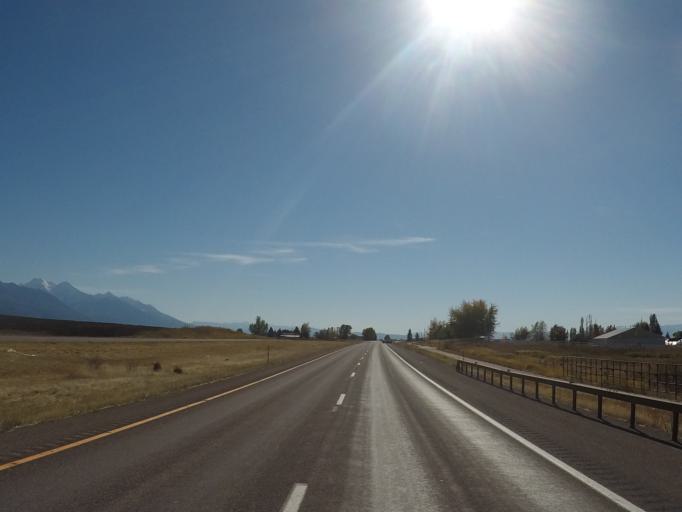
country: US
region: Montana
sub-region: Lake County
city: Pablo
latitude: 47.5744
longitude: -114.1134
